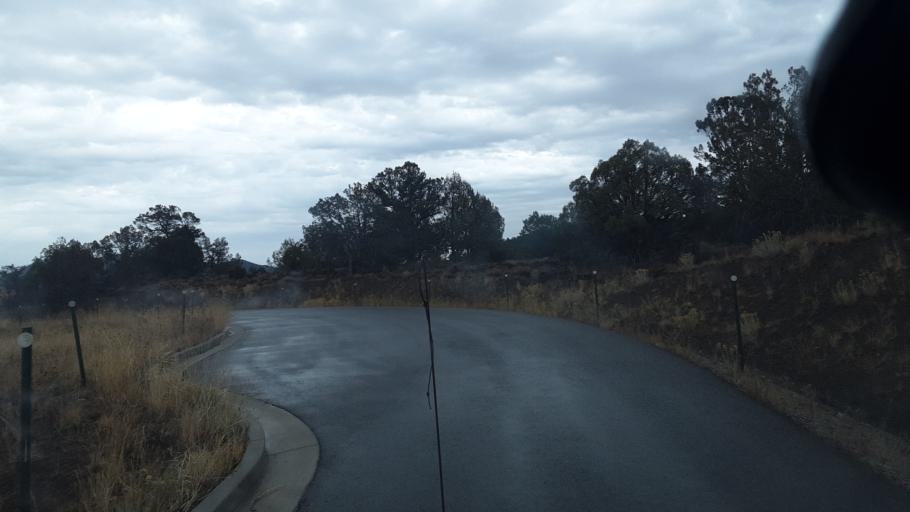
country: US
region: Colorado
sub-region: La Plata County
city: Durango
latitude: 37.2408
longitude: -107.9030
